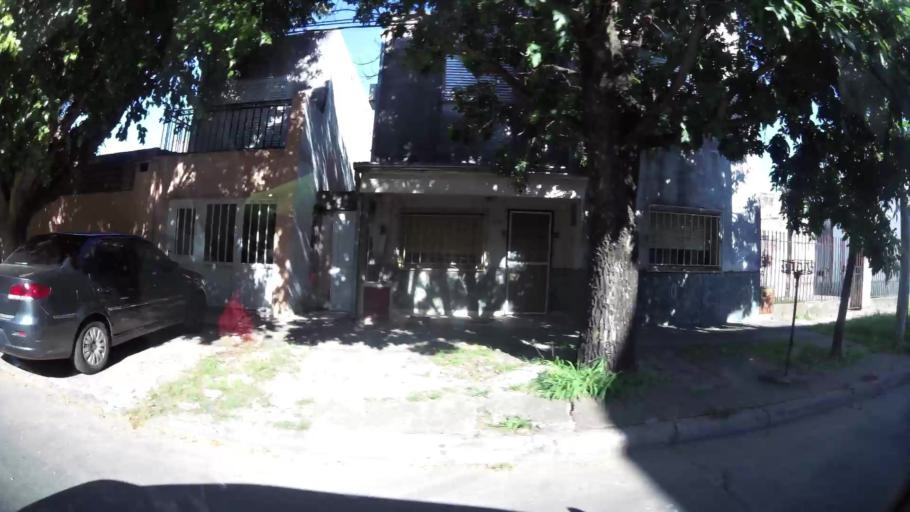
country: AR
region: Santa Fe
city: Santa Fe de la Vera Cruz
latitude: -31.6143
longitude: -60.6910
